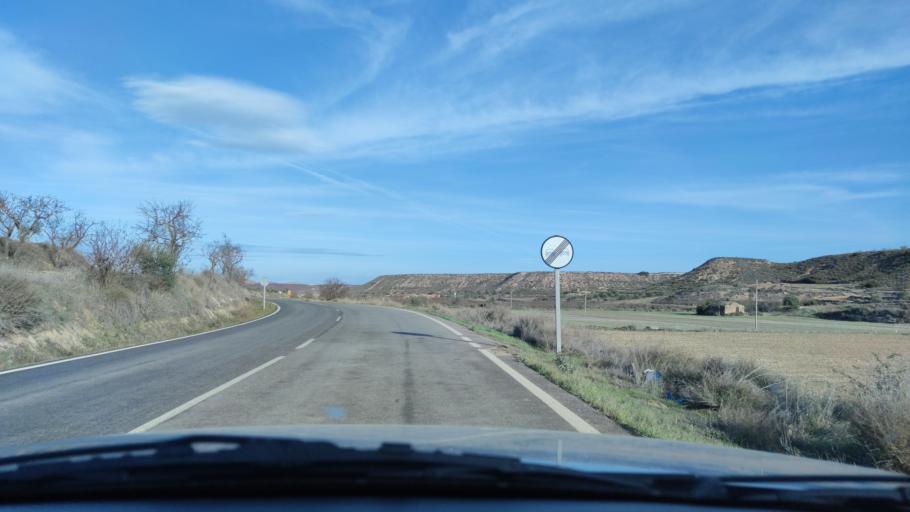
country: ES
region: Catalonia
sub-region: Provincia de Lleida
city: Alcano
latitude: 41.4876
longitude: 0.6160
